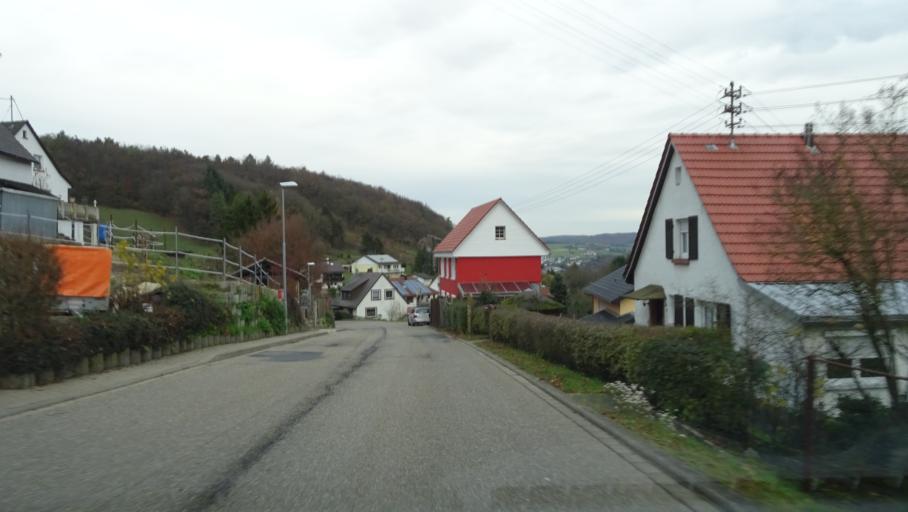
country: DE
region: Baden-Wuerttemberg
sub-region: Karlsruhe Region
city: Binau
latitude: 49.3569
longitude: 9.0421
